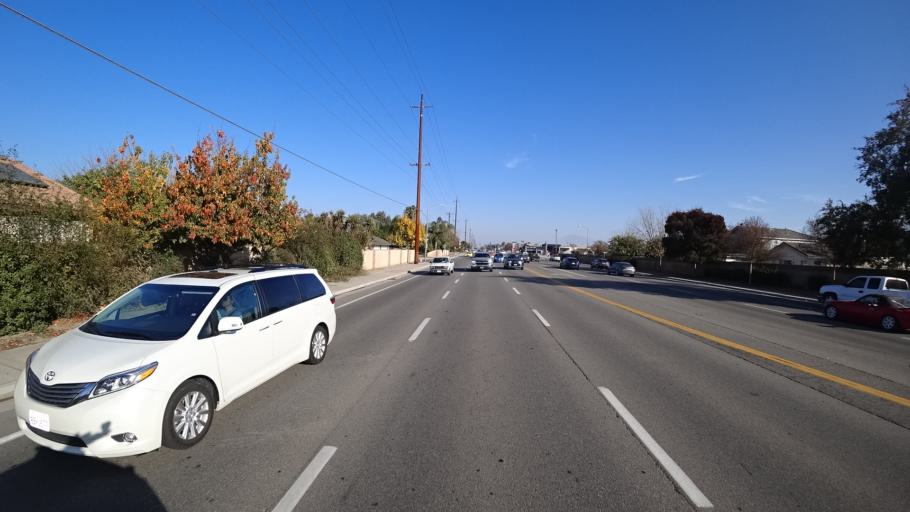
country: US
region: California
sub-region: Kern County
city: Greenfield
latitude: 35.2960
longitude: -119.0448
